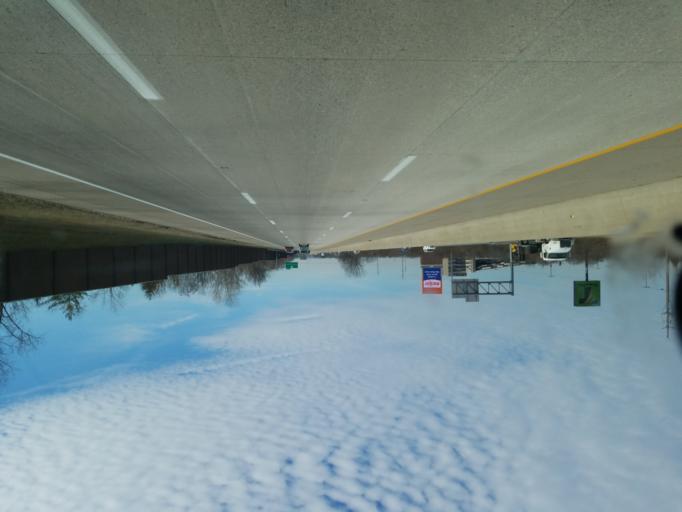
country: US
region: Ohio
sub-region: Montgomery County
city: Huber Heights
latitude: 39.8685
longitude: -84.1155
